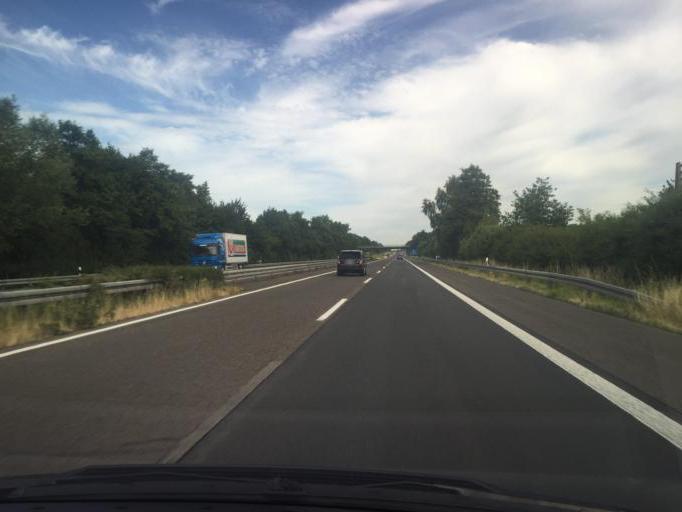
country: DE
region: North Rhine-Westphalia
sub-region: Regierungsbezirk Dusseldorf
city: Sonsbeck
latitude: 51.5951
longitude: 6.3664
